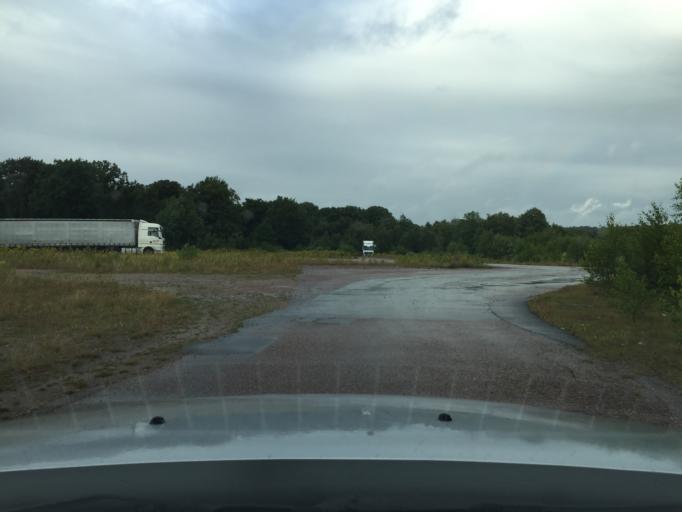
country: SE
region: Skane
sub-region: Hoors Kommun
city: Hoeoer
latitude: 55.9574
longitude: 13.5658
